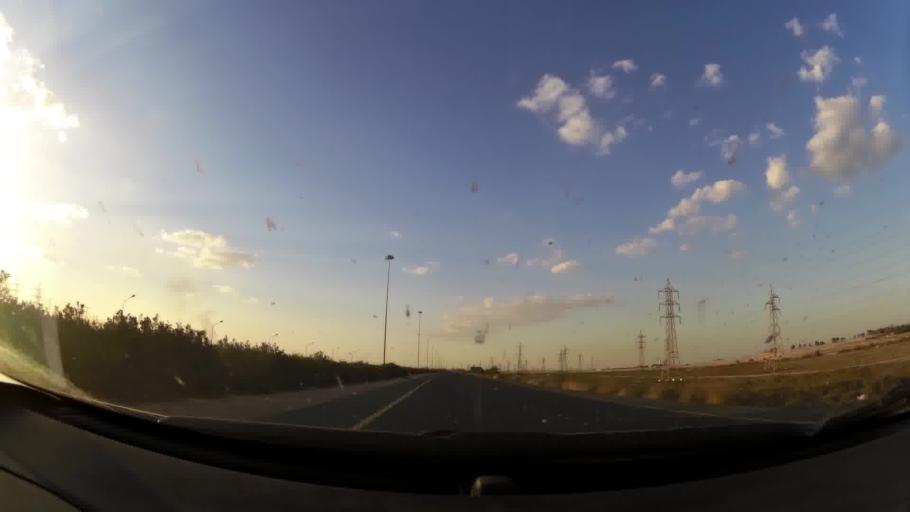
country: KW
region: Al Ahmadi
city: Al Fahahil
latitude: 28.9253
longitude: 48.2025
